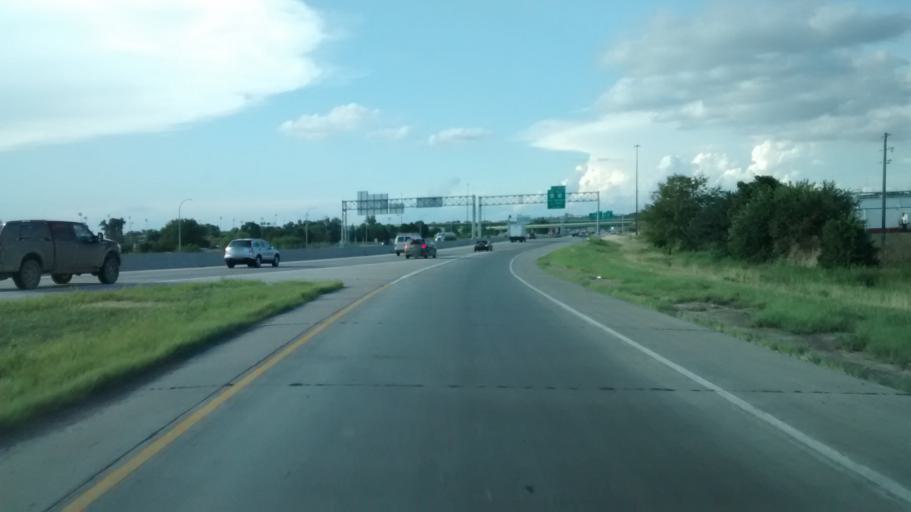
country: US
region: Iowa
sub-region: Woodbury County
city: Sergeant Bluff
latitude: 42.4373
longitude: -96.3750
